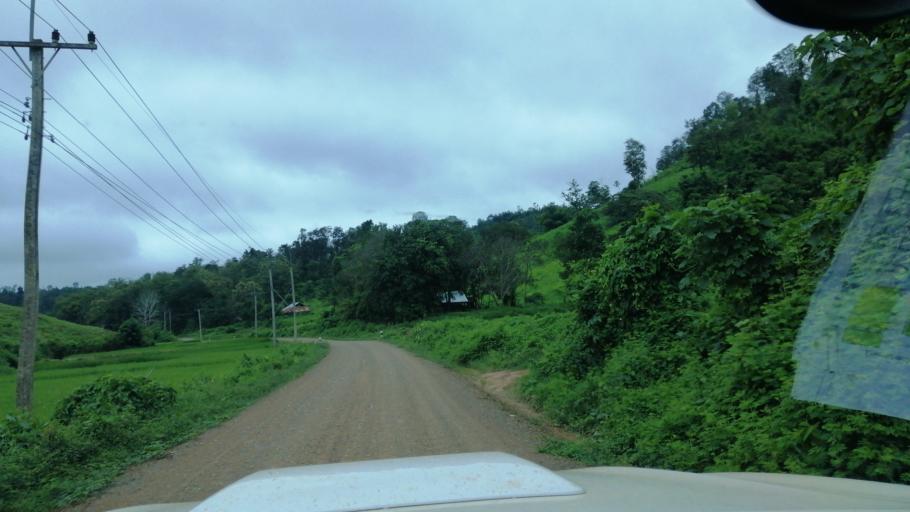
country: LA
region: Xiagnabouli
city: Muang Kenthao
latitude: 17.9389
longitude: 101.3907
